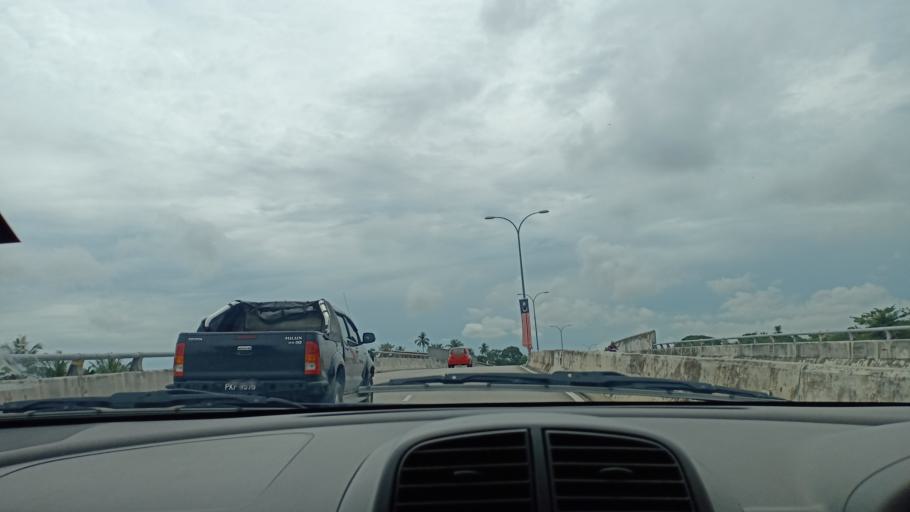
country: MY
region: Penang
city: Bukit Mertajam
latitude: 5.4065
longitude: 100.4737
